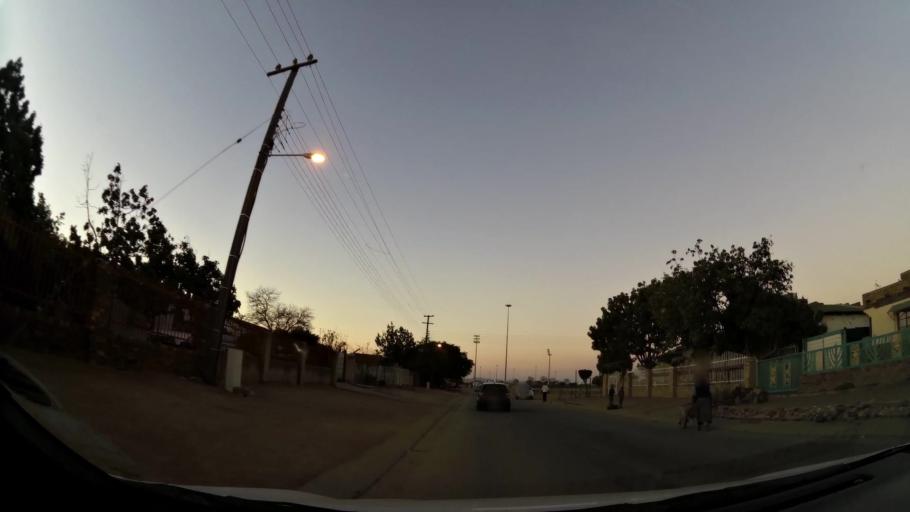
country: ZA
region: Limpopo
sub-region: Capricorn District Municipality
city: Polokwane
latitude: -23.8575
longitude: 29.3870
